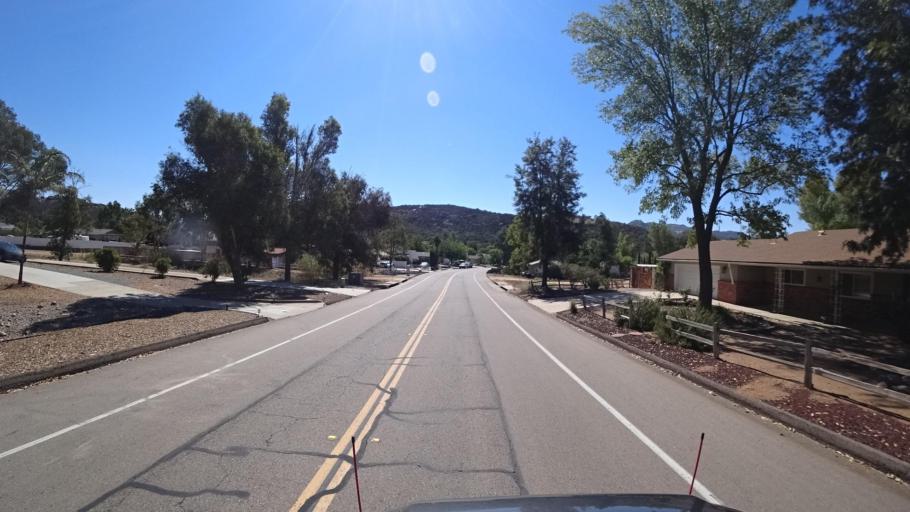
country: US
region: California
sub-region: San Diego County
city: San Diego Country Estates
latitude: 33.0127
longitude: -116.8130
